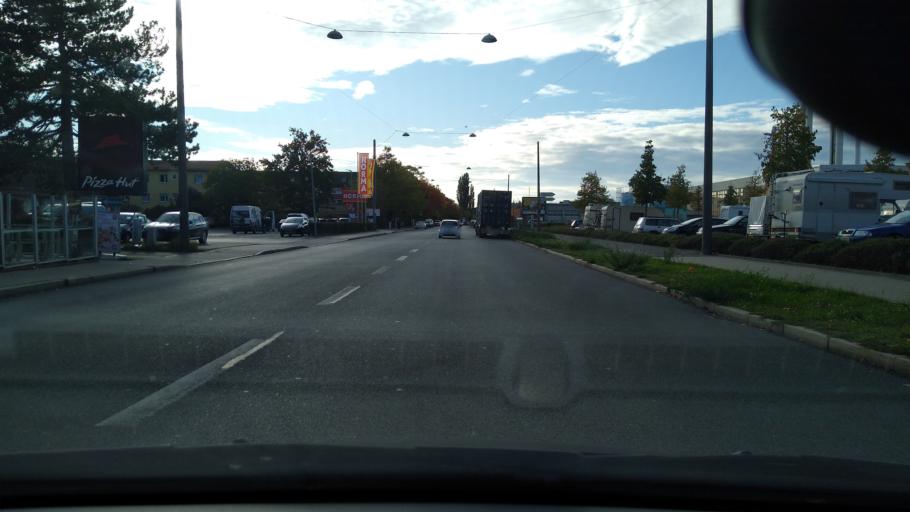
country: DE
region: Bavaria
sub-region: Regierungsbezirk Mittelfranken
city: Furth
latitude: 49.4588
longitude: 11.0024
